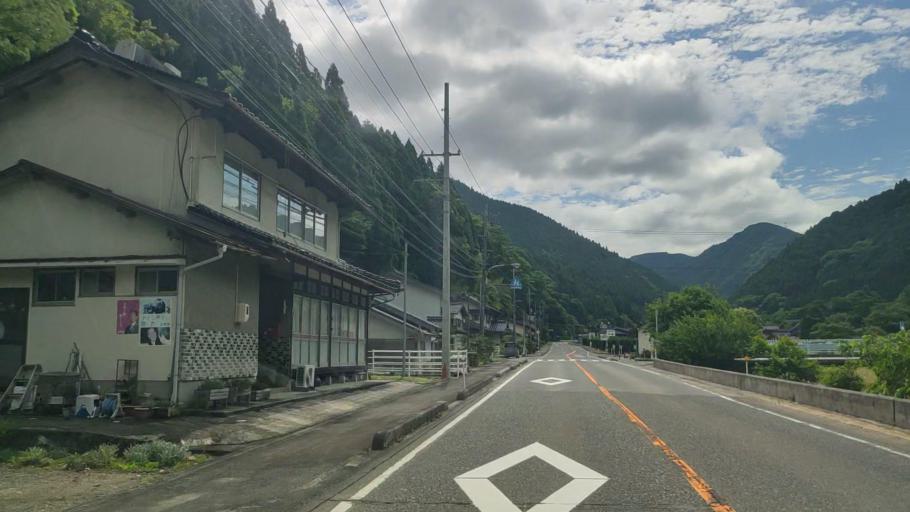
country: JP
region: Okayama
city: Niimi
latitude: 35.2179
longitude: 133.4554
